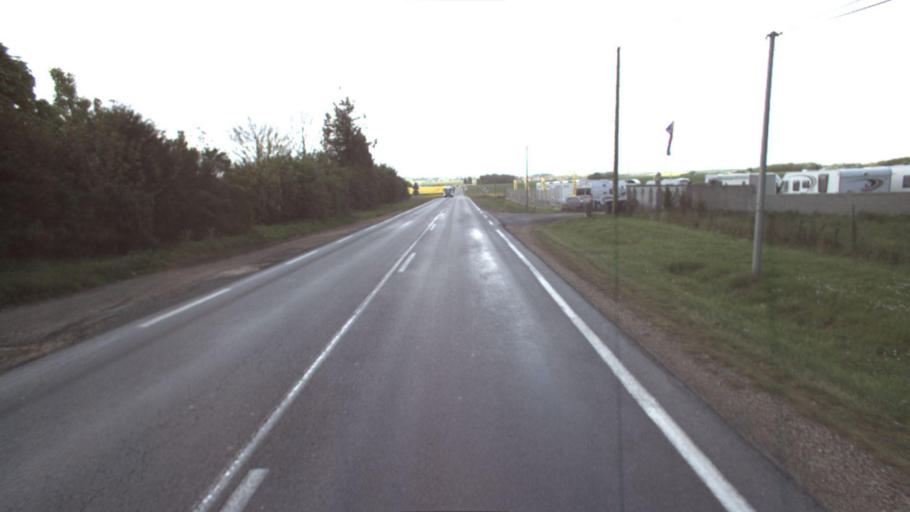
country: FR
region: Ile-de-France
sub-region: Departement de Seine-et-Marne
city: Jouy-le-Chatel
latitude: 48.6882
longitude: 3.1243
